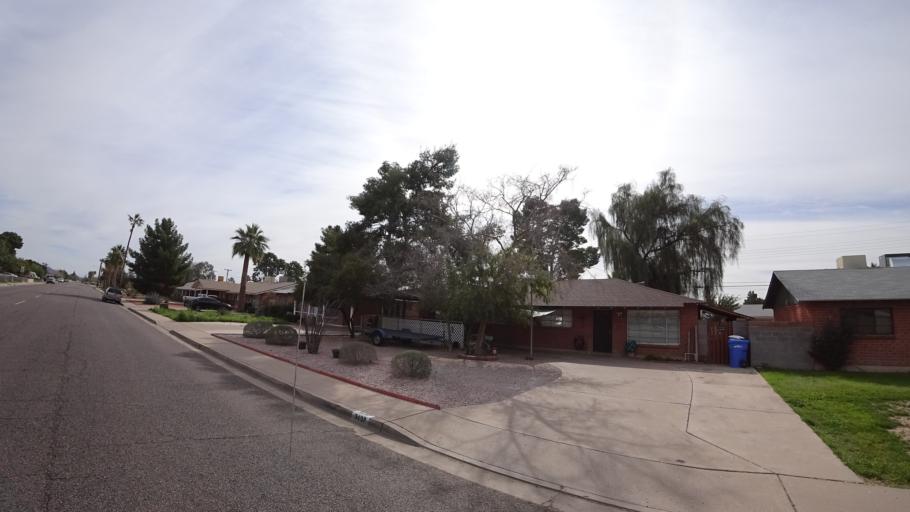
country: US
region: Arizona
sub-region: Maricopa County
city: Glendale
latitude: 33.5312
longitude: -112.1277
